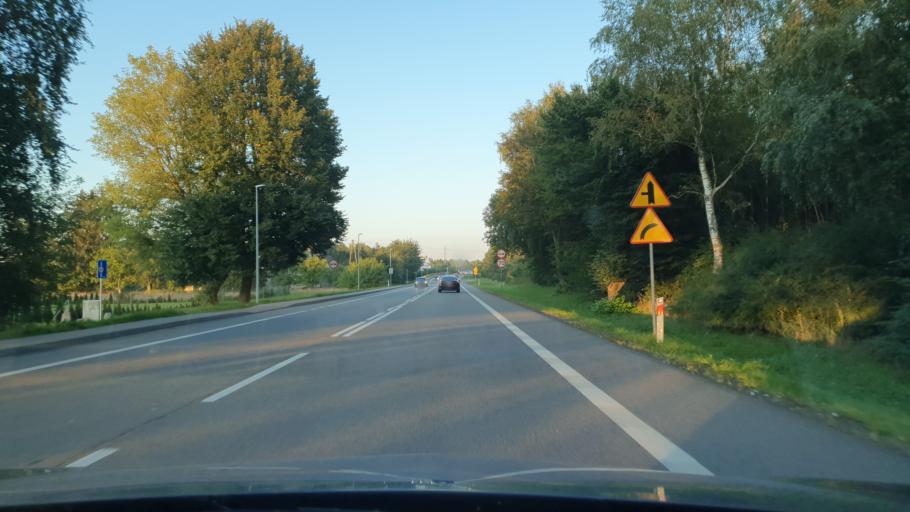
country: PL
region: Pomeranian Voivodeship
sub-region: Powiat slupski
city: Potegowo
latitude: 54.4744
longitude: 17.4863
